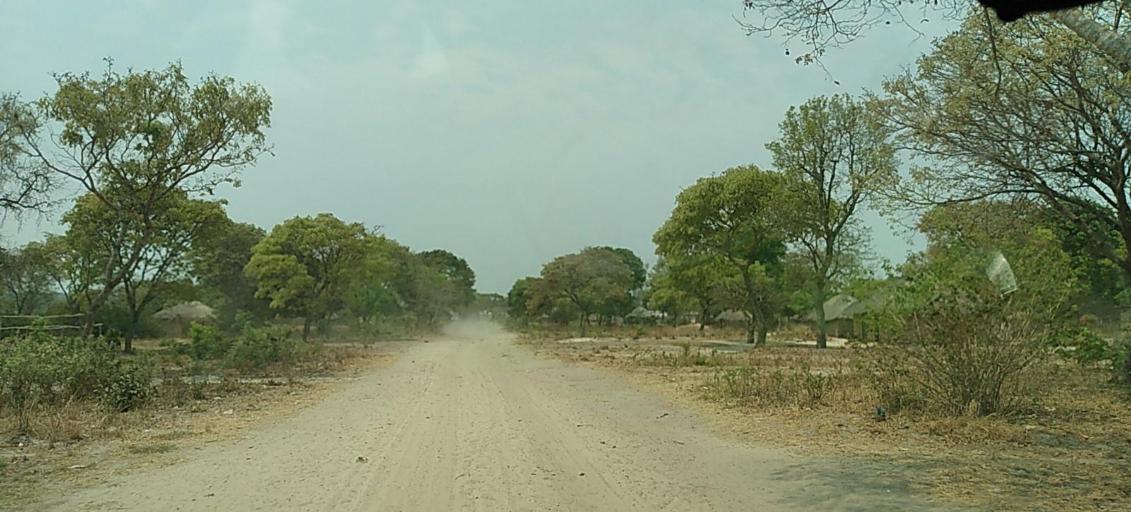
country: ZM
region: North-Western
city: Kabompo
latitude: -13.4923
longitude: 24.4642
